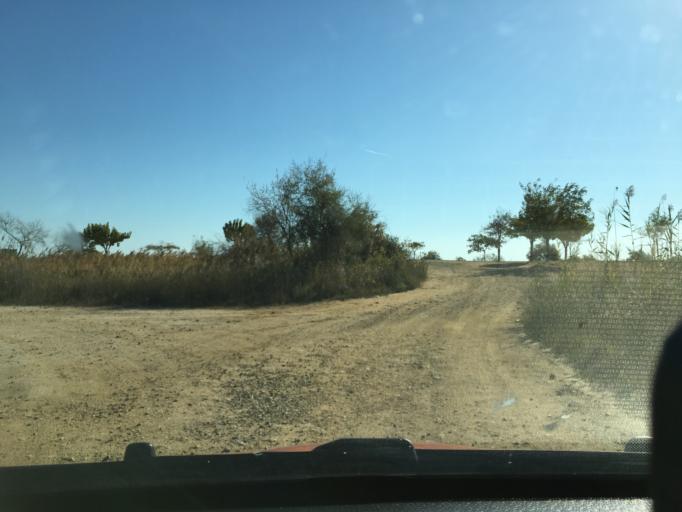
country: GR
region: Central Macedonia
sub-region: Nomos Chalkidikis
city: Nea Potidhaia
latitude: 40.2121
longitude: 23.3301
